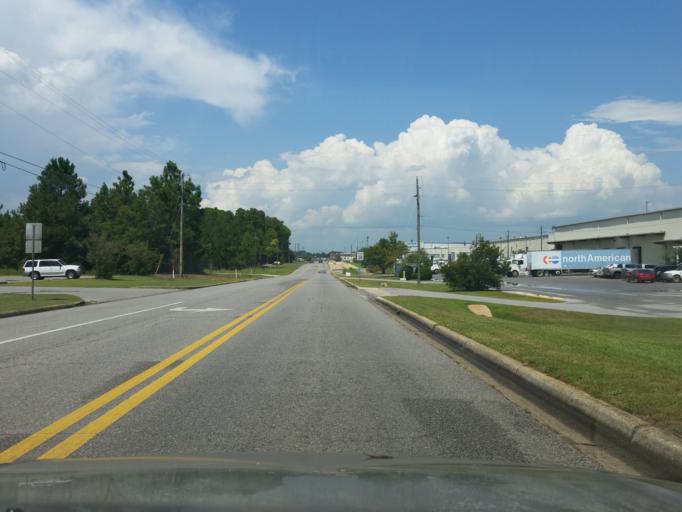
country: US
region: Florida
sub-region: Escambia County
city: Ferry Pass
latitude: 30.5176
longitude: -87.2016
